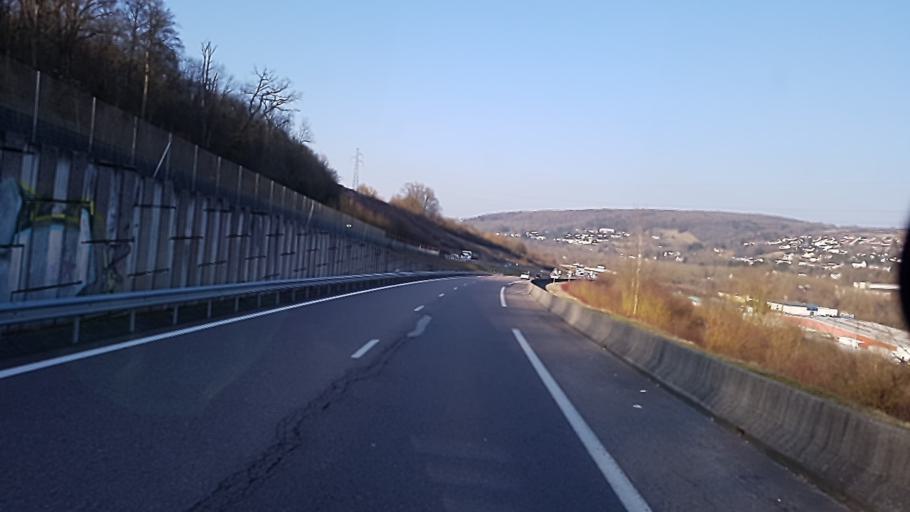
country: DE
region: Saarland
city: Kleinblittersdorf
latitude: 49.1351
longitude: 7.0387
